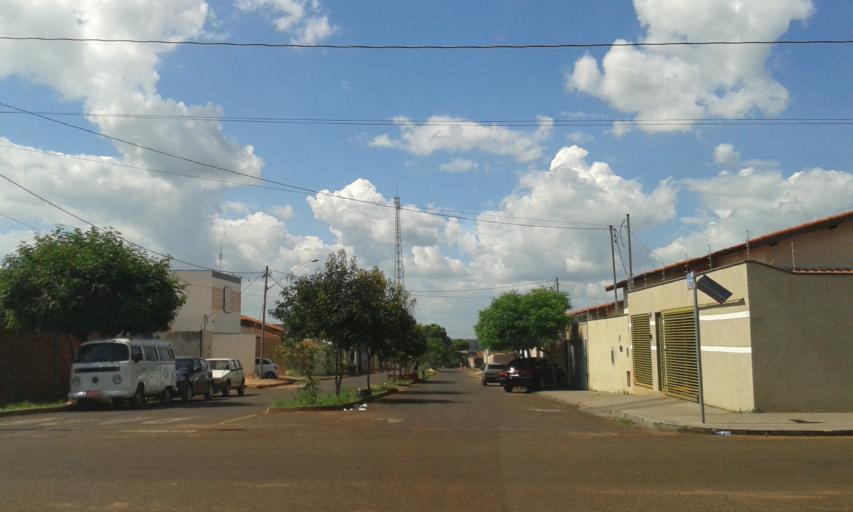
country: BR
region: Minas Gerais
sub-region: Santa Vitoria
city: Santa Vitoria
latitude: -18.8507
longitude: -50.1230
